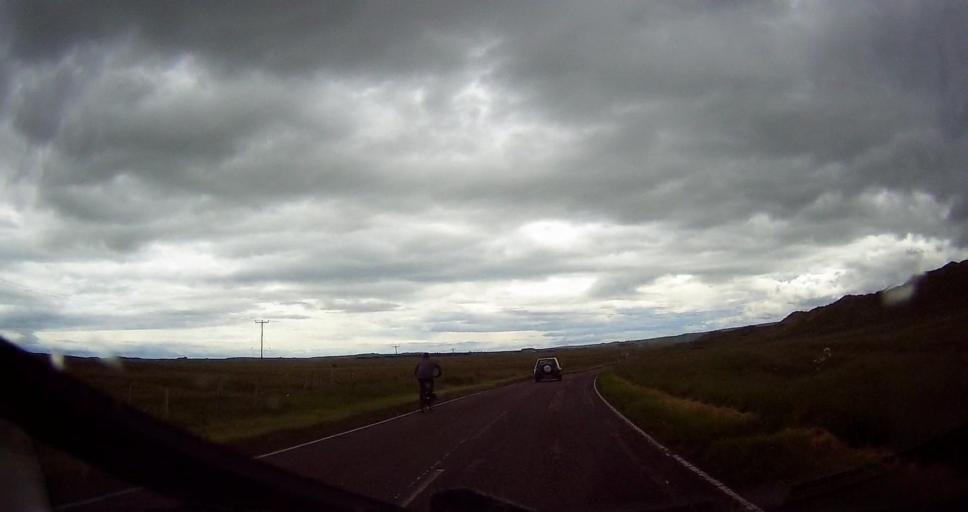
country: GB
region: Scotland
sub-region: Highland
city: Thurso
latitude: 58.6078
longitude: -3.3441
